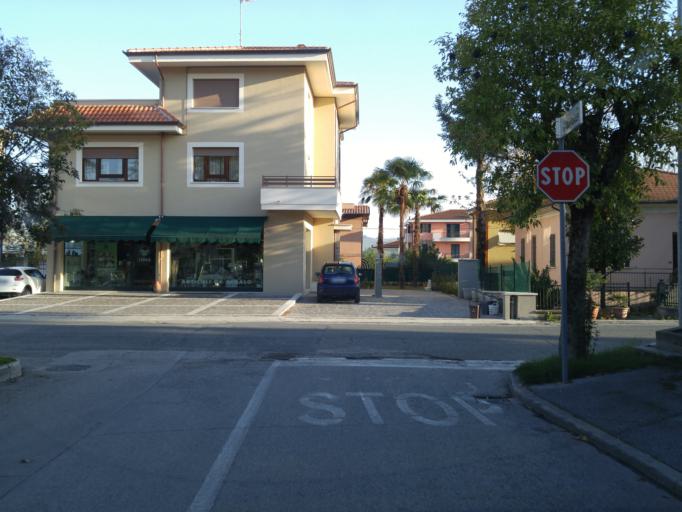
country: IT
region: The Marches
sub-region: Provincia di Pesaro e Urbino
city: Calcinelli
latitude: 43.7498
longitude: 12.9168
